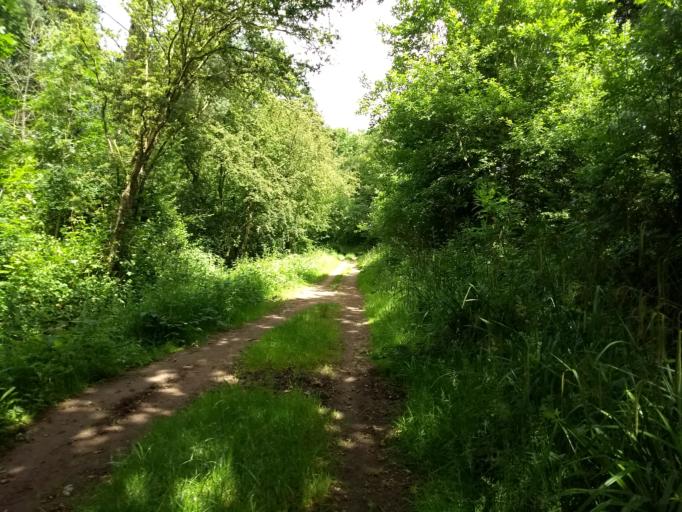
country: GB
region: England
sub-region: Milton Keynes
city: Shenley Church End
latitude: 52.0106
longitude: -0.8116
